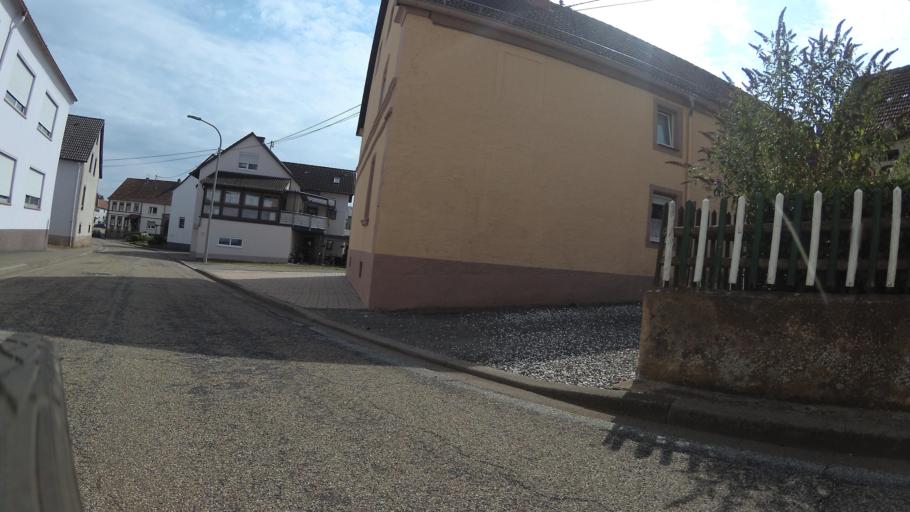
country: DE
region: Rheinland-Pfalz
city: Wahnwegen
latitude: 49.4862
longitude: 7.3745
